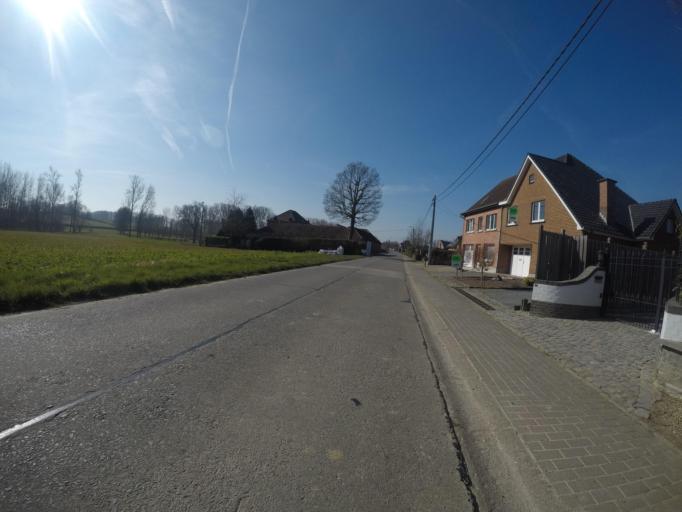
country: BE
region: Flanders
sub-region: Provincie Oost-Vlaanderen
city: Geraardsbergen
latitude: 50.7955
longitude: 3.8669
